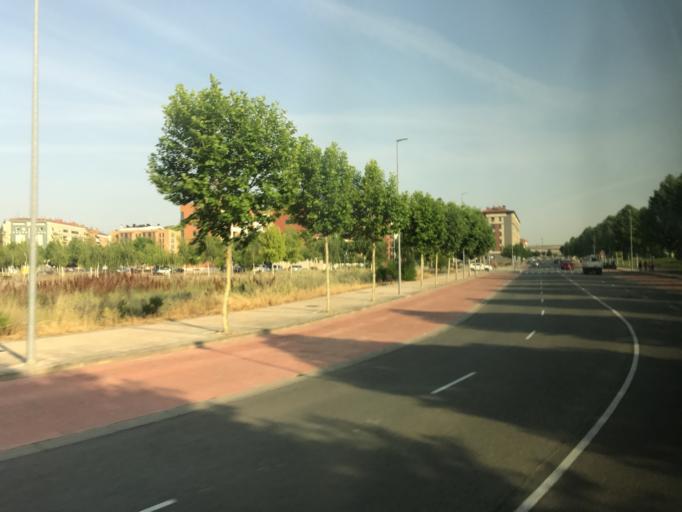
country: ES
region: Castille and Leon
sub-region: Provincia de Burgos
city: Miranda de Ebro
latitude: 42.6863
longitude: -2.9309
